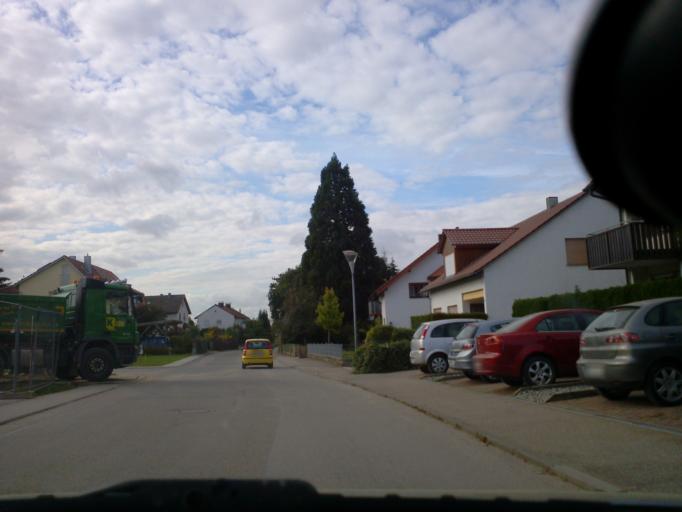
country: DE
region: Baden-Wuerttemberg
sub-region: Regierungsbezirk Stuttgart
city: Gemmingen
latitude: 49.1549
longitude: 8.9806
